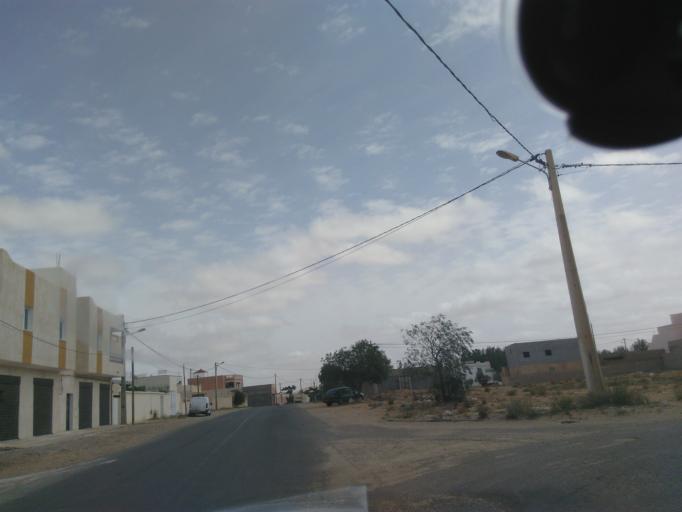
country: TN
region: Tataouine
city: Tataouine
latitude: 32.9546
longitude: 10.4649
